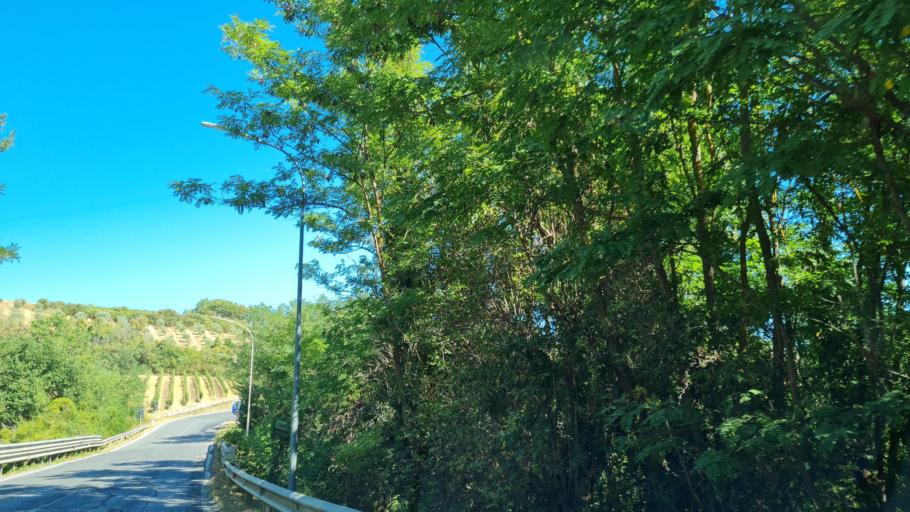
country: IT
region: Tuscany
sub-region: Provincia di Siena
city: Sant'Albino
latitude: 43.0734
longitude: 11.8001
